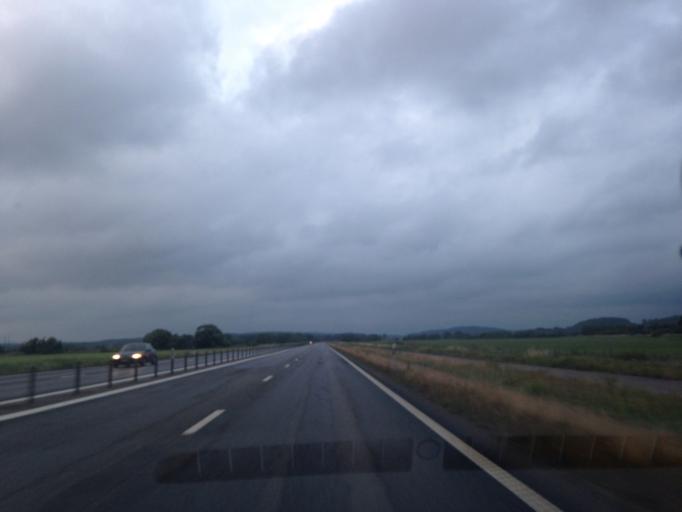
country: SE
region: Halland
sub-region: Varbergs Kommun
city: Varberg
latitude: 57.1312
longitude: 12.2618
